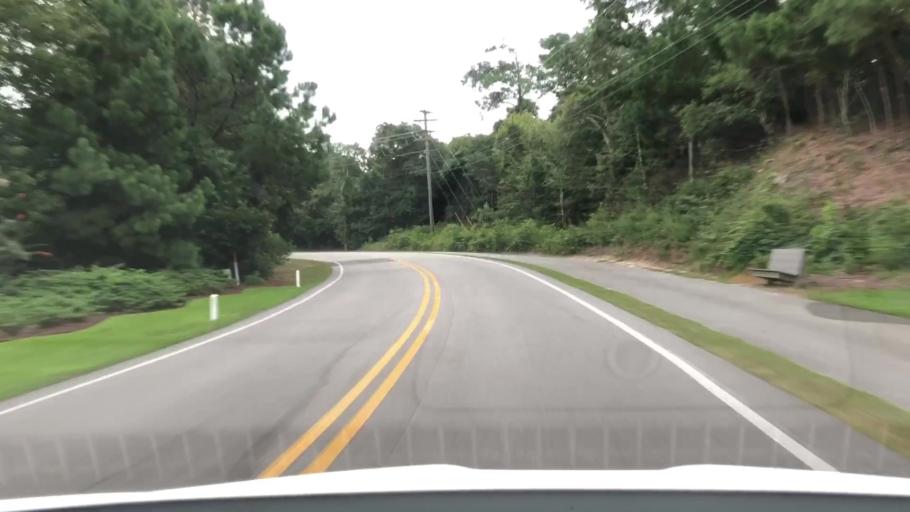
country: US
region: North Carolina
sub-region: Carteret County
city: Cedar Point
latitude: 34.6570
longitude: -77.0742
